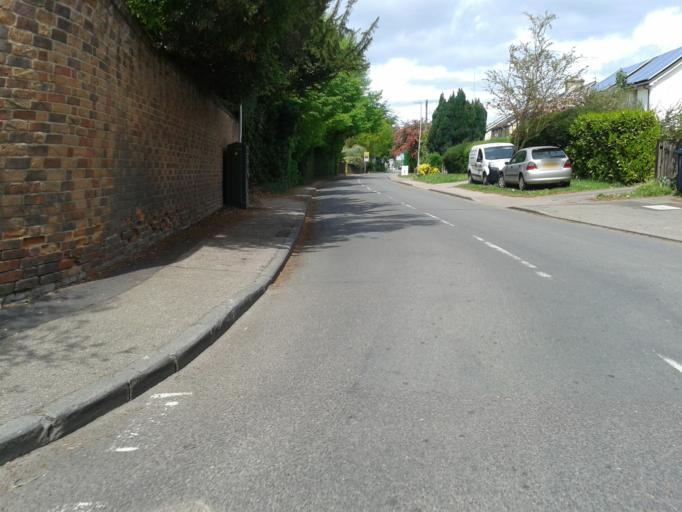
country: GB
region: England
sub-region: Cambridgeshire
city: Meldreth
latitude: 52.1126
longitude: 0.0329
